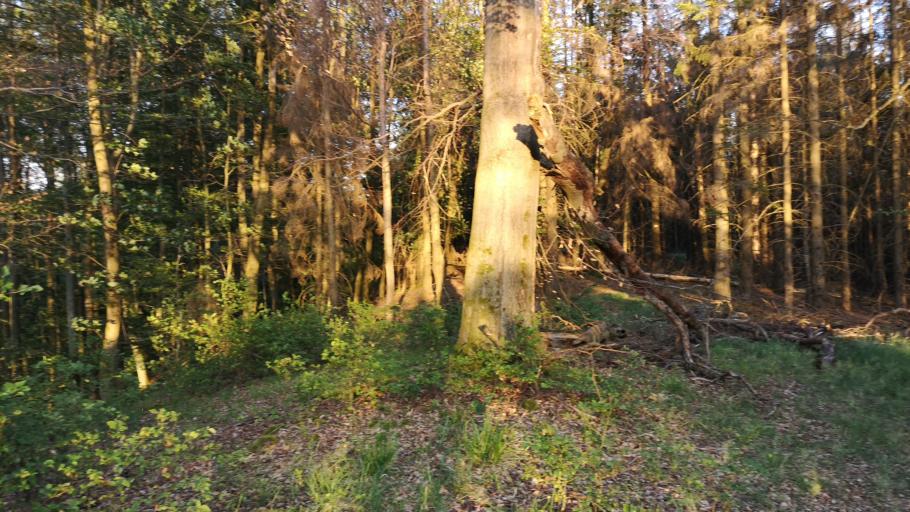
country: DE
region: Saxony-Anhalt
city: Stolberg
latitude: 51.5758
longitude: 10.9701
